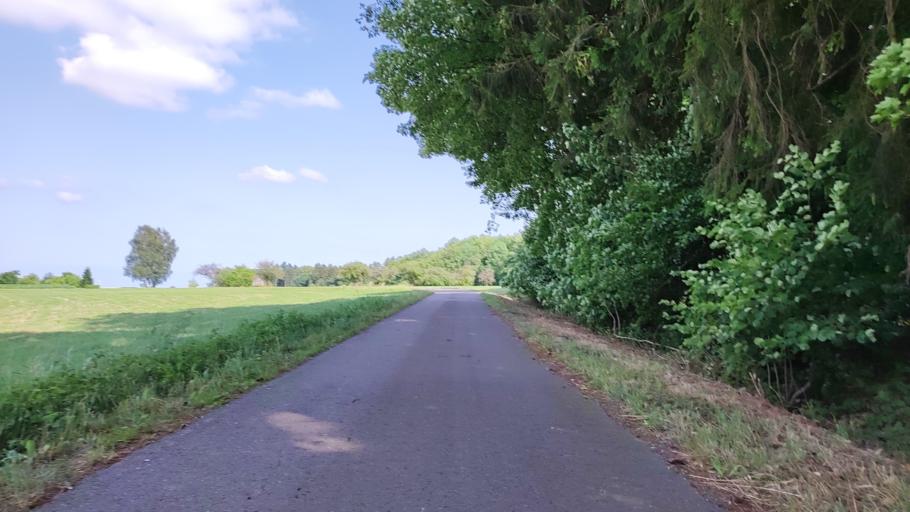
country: DE
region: Bavaria
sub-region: Swabia
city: Holzheim
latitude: 48.4942
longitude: 10.5566
